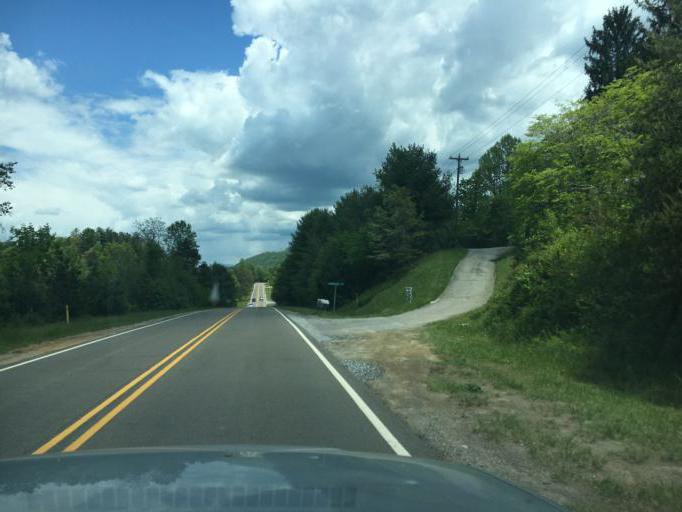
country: US
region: North Carolina
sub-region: Buncombe County
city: Weaverville
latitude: 35.7175
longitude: -82.5591
